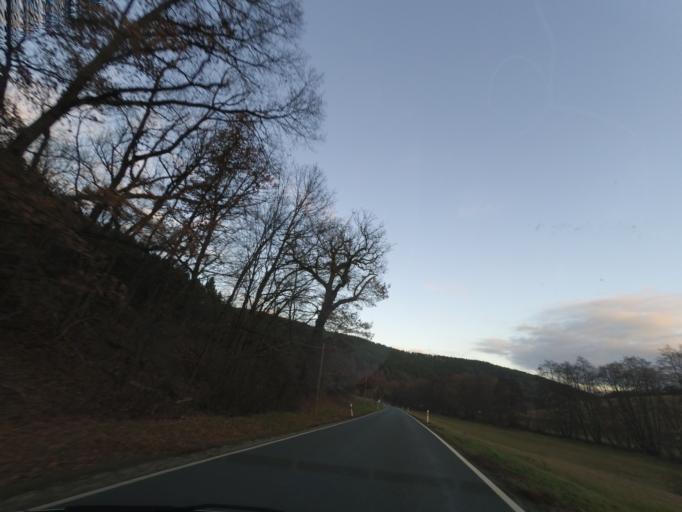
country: DE
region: Thuringia
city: Rottenbach
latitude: 50.6969
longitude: 11.1270
